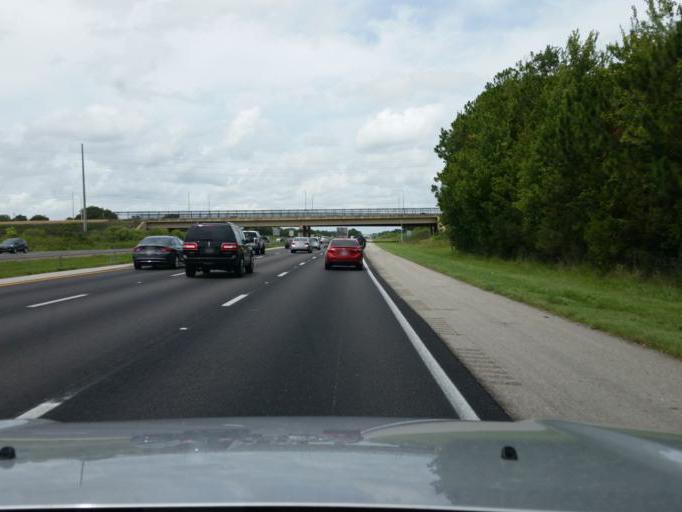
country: US
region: Florida
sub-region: Polk County
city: Loughman
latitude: 28.2561
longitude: -81.6174
